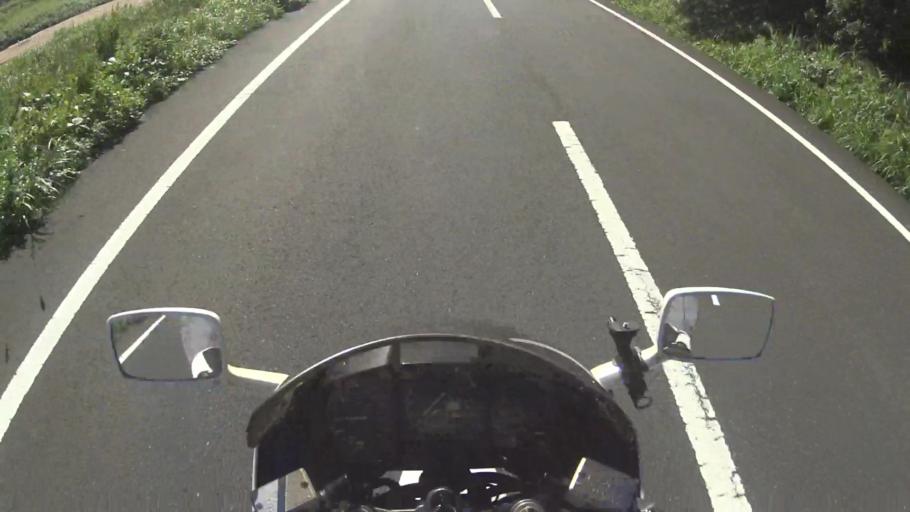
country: JP
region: Kyoto
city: Miyazu
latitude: 35.7043
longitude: 135.1027
